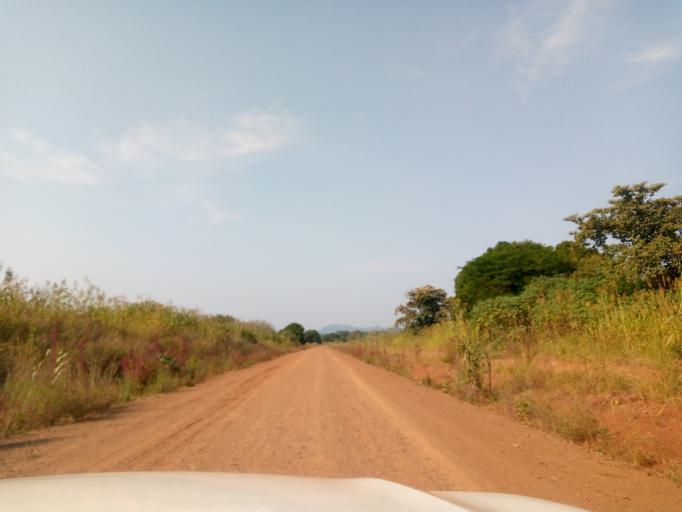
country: ET
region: Oromiya
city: Mendi
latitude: 10.1408
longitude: 34.9475
